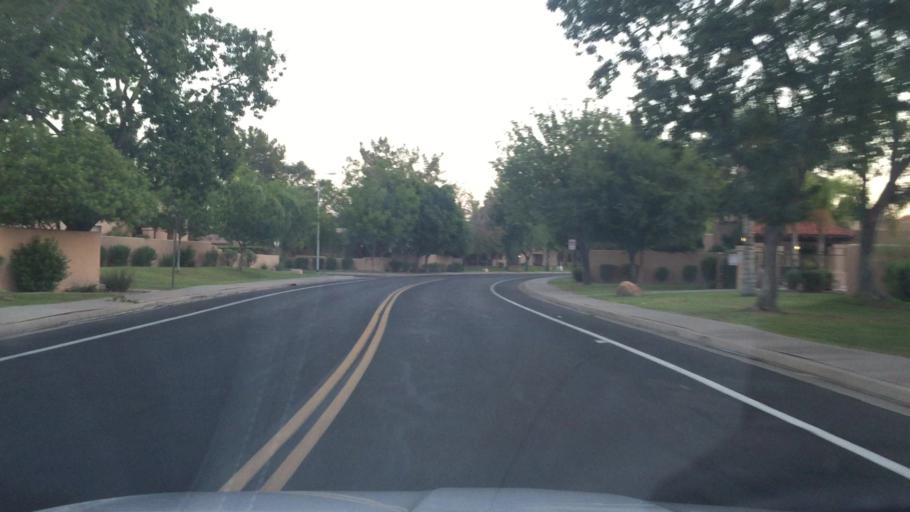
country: US
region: Arizona
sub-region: Maricopa County
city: Scottsdale
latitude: 33.5204
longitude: -111.9133
